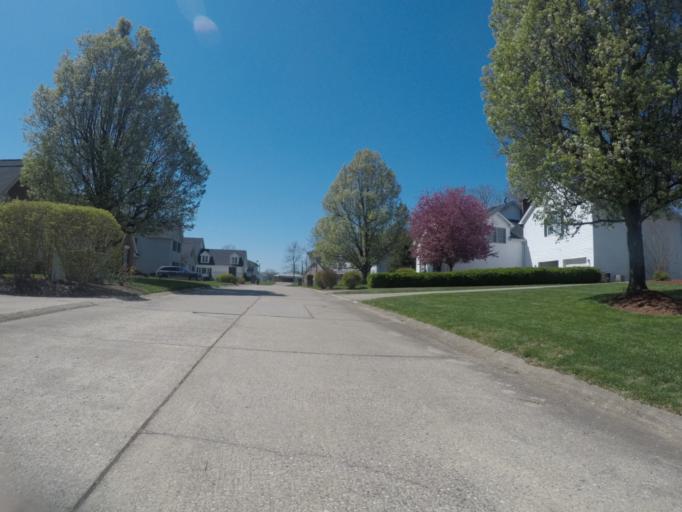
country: US
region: West Virginia
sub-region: Cabell County
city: Pea Ridge
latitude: 38.4223
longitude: -82.3169
